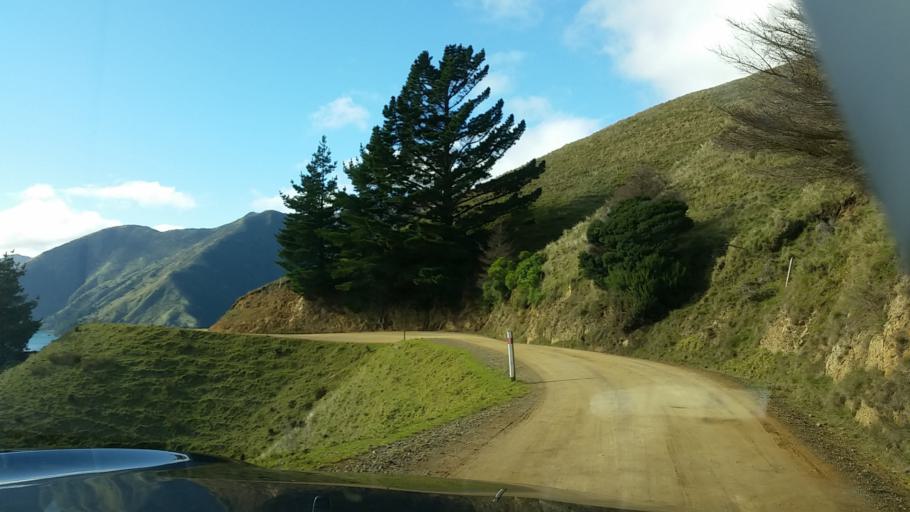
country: NZ
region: Marlborough
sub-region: Marlborough District
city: Picton
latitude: -40.9856
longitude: 173.8400
